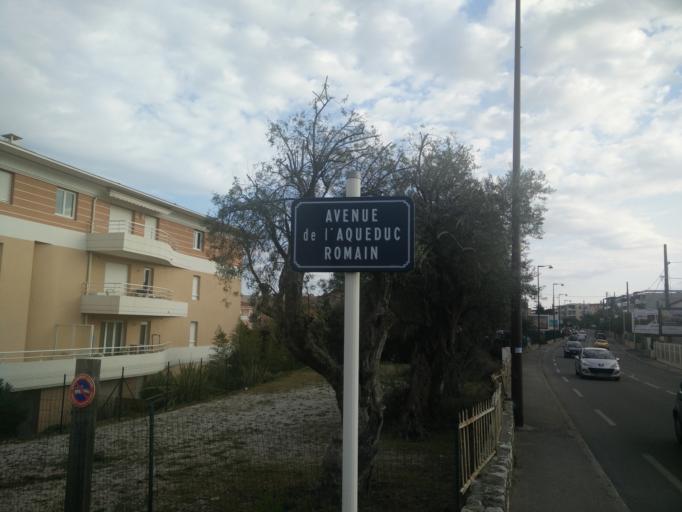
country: FR
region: Provence-Alpes-Cote d'Azur
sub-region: Departement des Alpes-Maritimes
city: Antibes
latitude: 43.5962
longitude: 7.1201
